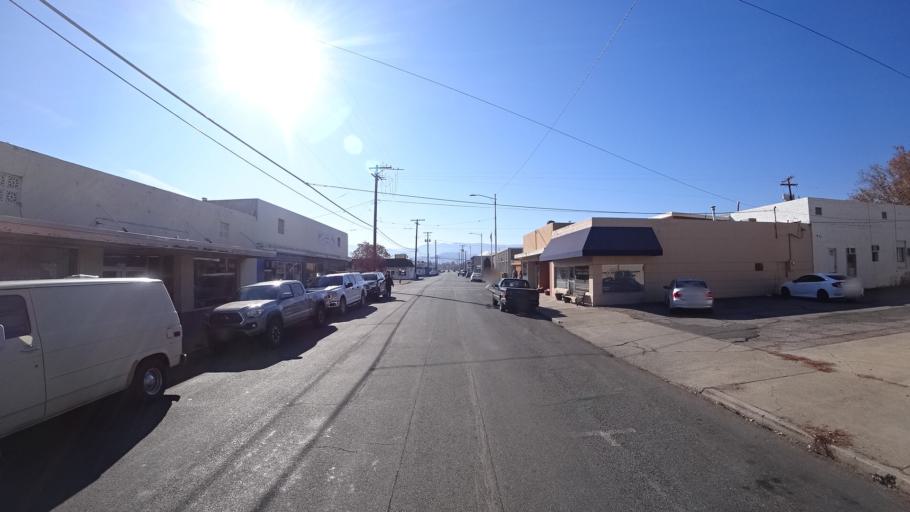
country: US
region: California
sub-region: Siskiyou County
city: Yreka
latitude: 41.7298
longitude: -122.6370
